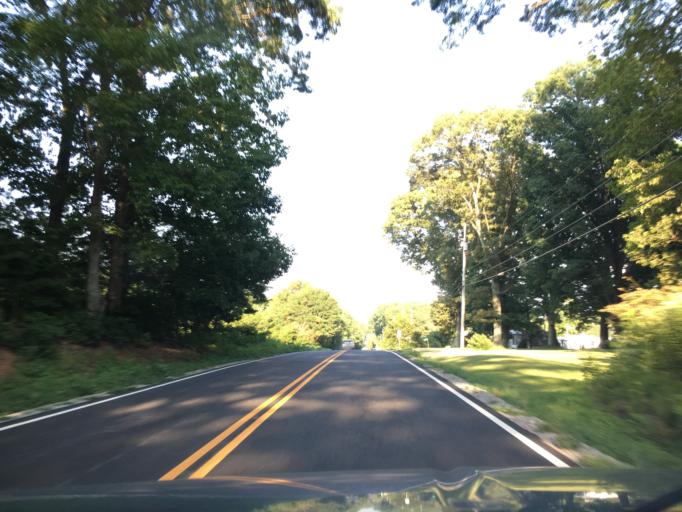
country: US
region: Virginia
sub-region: Pittsylvania County
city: Chatham
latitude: 36.8198
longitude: -79.3717
